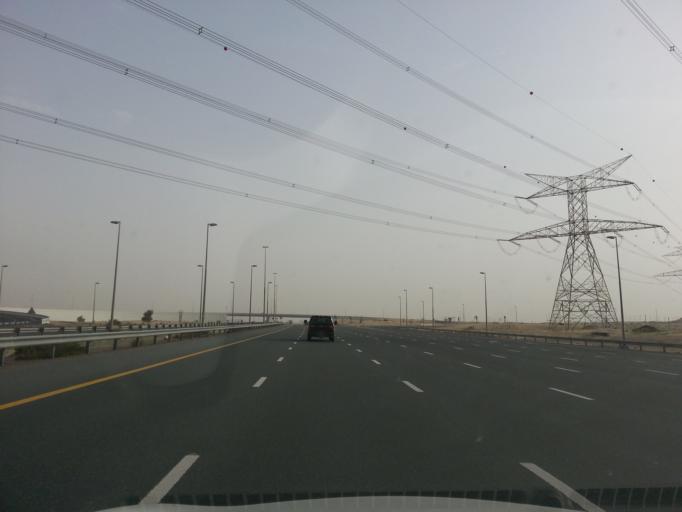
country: AE
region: Dubai
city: Dubai
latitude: 24.9832
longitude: 55.2428
